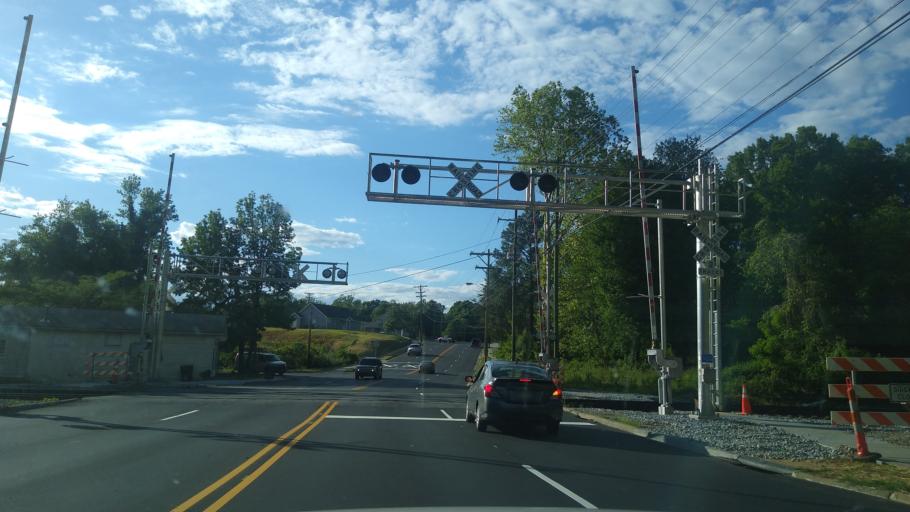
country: US
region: North Carolina
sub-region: Guilford County
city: Greensboro
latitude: 36.1260
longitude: -79.7731
